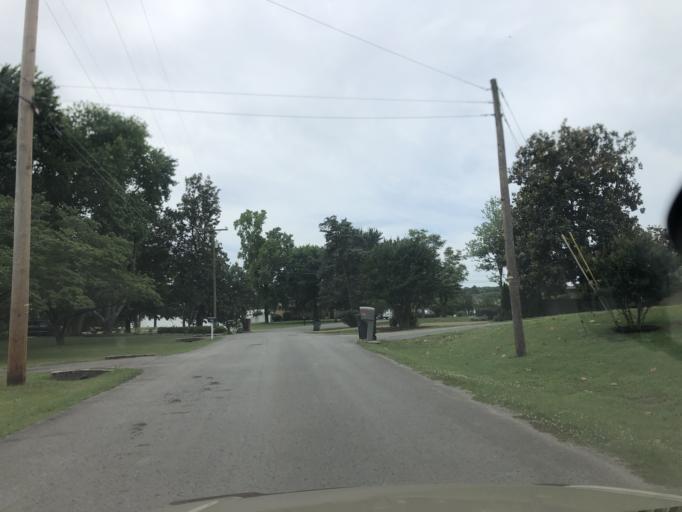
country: US
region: Tennessee
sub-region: Davidson County
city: Lakewood
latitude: 36.2507
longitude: -86.6112
